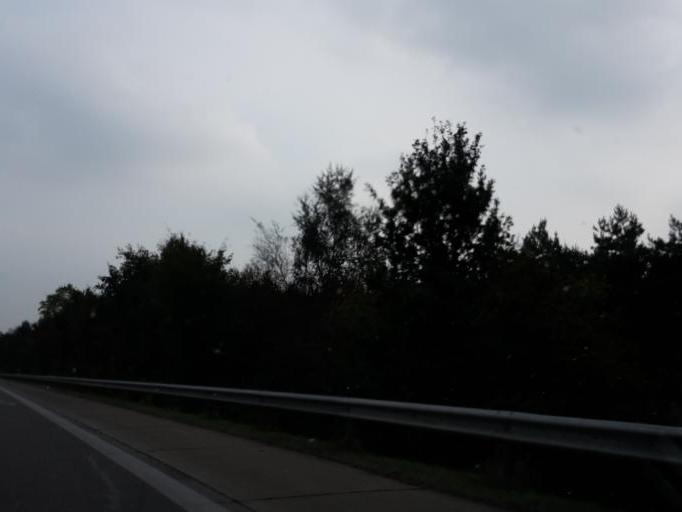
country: DE
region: Lower Saxony
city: Emstek
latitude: 52.8853
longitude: 8.1858
